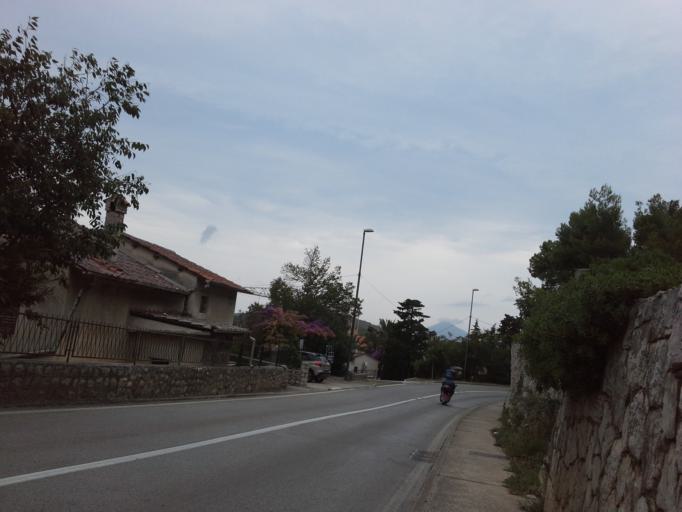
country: HR
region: Primorsko-Goranska
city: Mali Losinj
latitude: 44.5390
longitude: 14.4663
